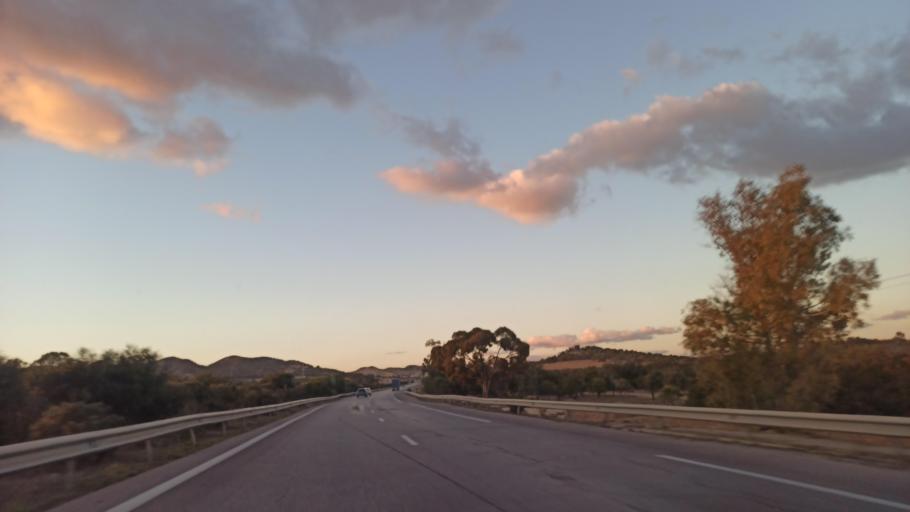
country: TN
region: Susah
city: Harqalah
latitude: 36.2164
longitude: 10.4203
